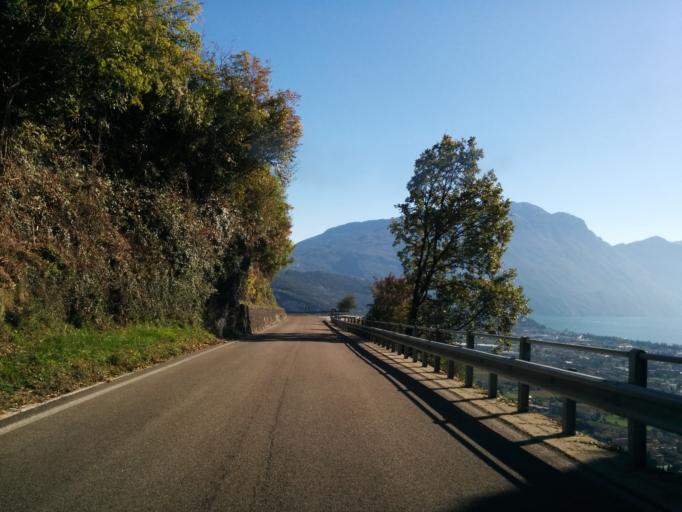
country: IT
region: Trentino-Alto Adige
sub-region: Provincia di Trento
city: Tenno
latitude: 45.9163
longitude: 10.8433
